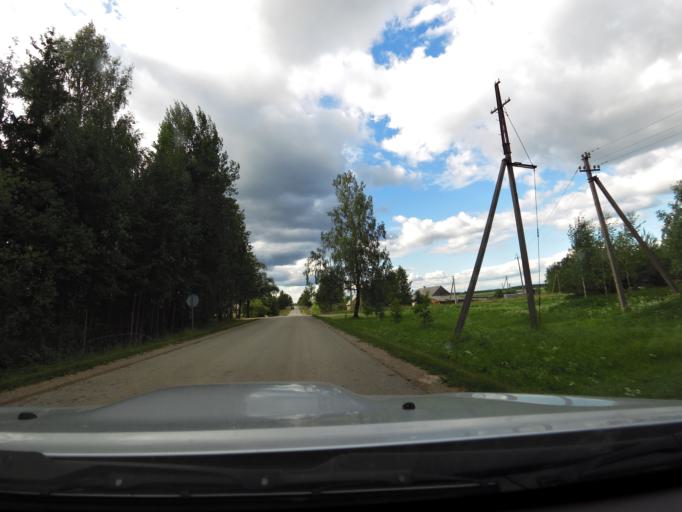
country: LT
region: Panevezys
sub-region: Birzai
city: Birzai
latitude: 56.3773
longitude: 24.7769
